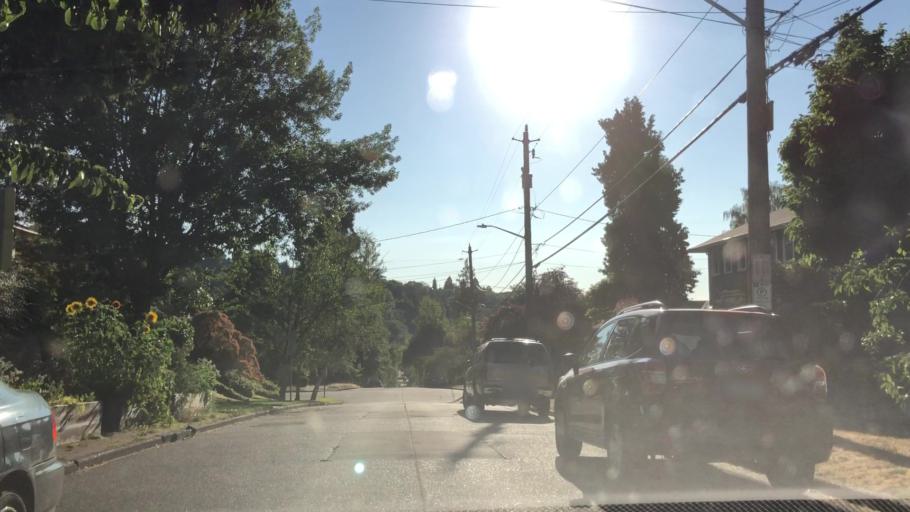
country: US
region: Washington
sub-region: King County
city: Seattle
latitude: 47.6395
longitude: -122.3046
